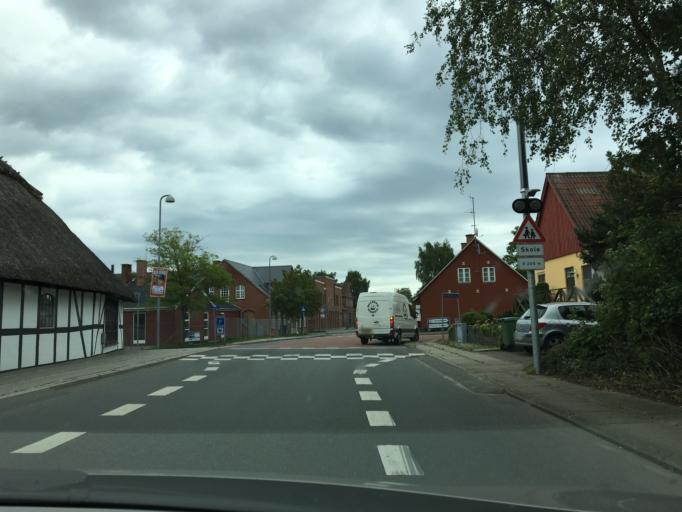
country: DK
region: South Denmark
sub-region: Svendborg Kommune
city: Thuro By
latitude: 55.0486
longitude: 10.6631
